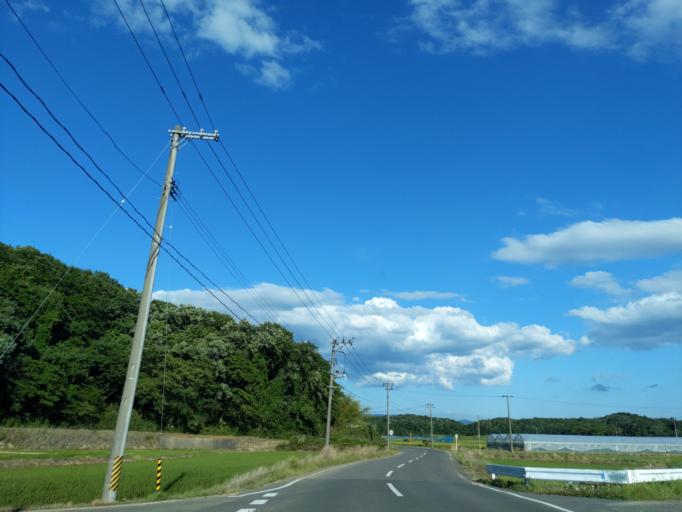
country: JP
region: Fukushima
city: Sukagawa
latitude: 37.3251
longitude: 140.3452
